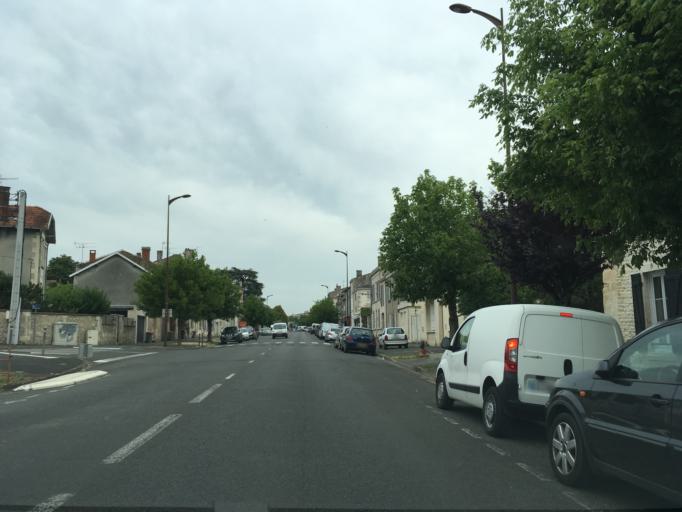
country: FR
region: Poitou-Charentes
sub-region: Departement des Deux-Sevres
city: Niort
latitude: 46.3179
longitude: -0.4706
